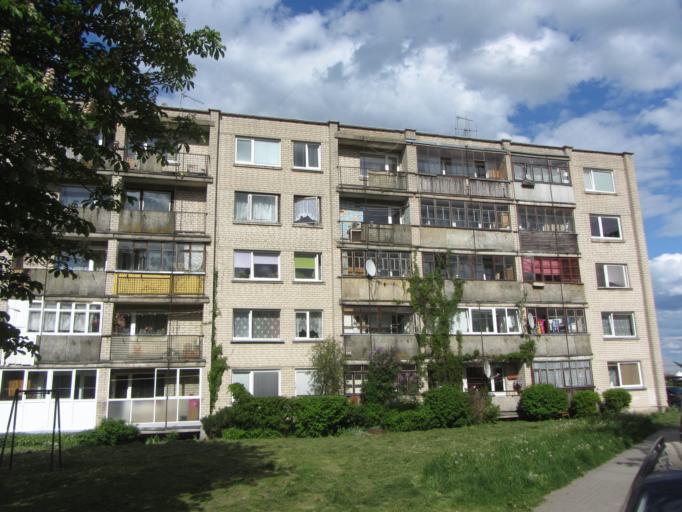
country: LT
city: Sirvintos
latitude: 55.0411
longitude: 24.9568
